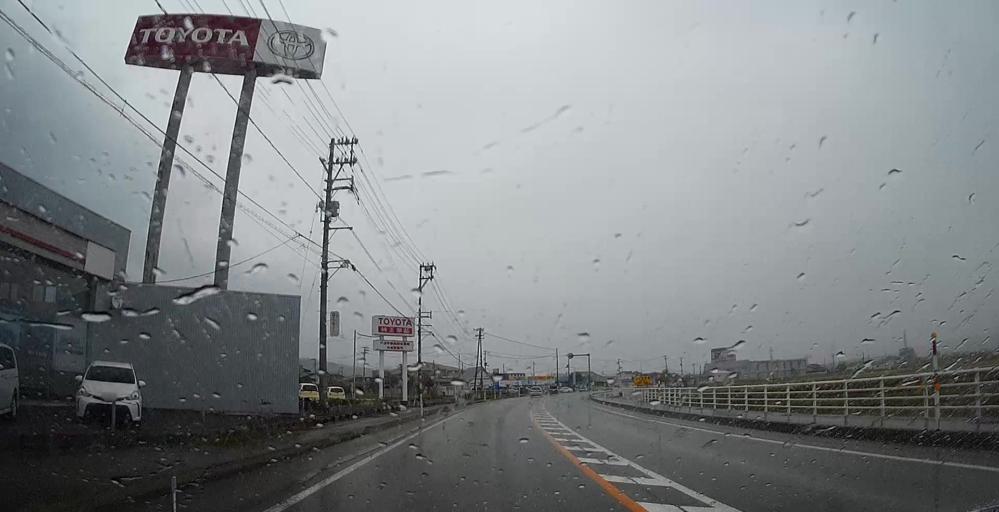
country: JP
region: Niigata
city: Kashiwazaki
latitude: 37.3864
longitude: 138.5850
